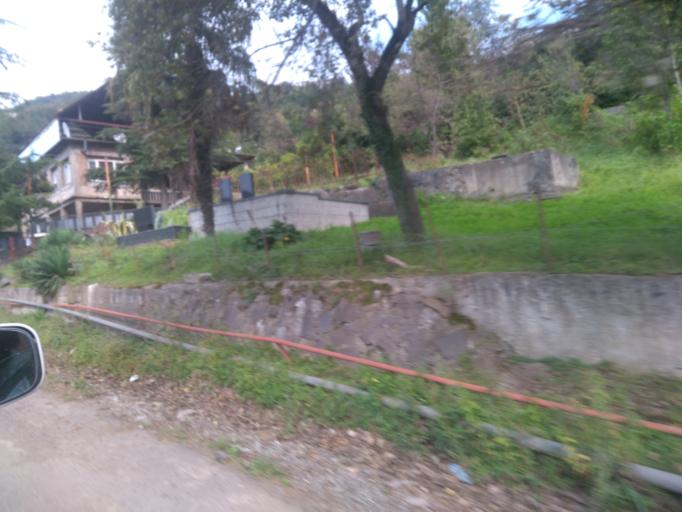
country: GE
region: Ajaria
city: Khelvachauri
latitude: 41.5608
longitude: 41.6930
